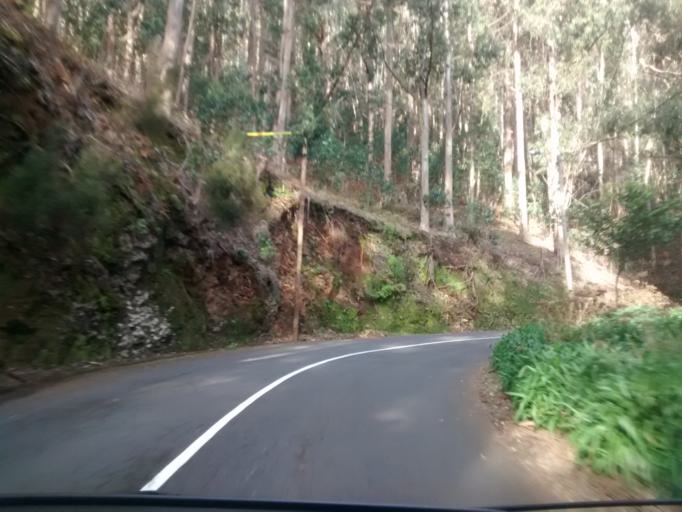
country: PT
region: Madeira
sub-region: Sao Vicente
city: Sao Vicente
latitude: 32.7466
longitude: -17.0260
